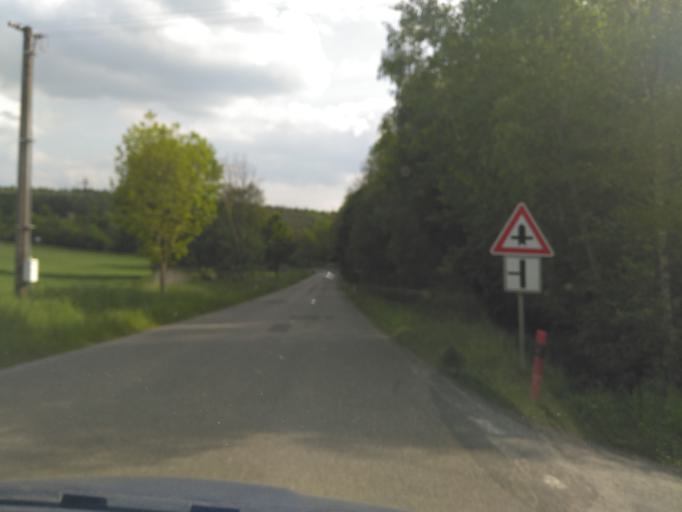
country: CZ
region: Central Bohemia
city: Chynava
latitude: 49.9972
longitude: 14.0922
